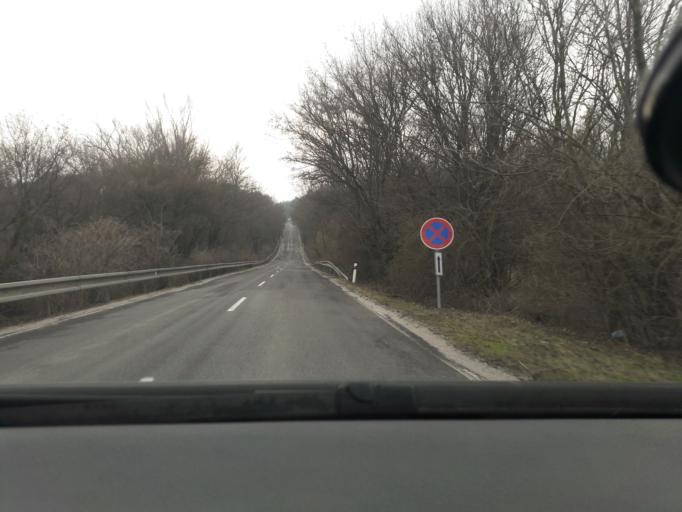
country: SK
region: Trnavsky
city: Smolenice
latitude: 48.4825
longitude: 17.4297
